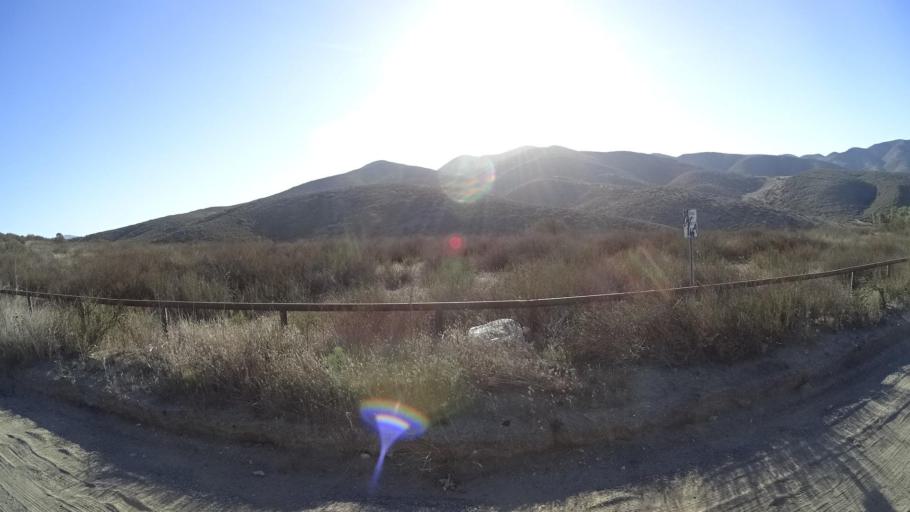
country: US
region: California
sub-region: San Diego County
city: Jamul
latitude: 32.6872
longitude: -116.9102
